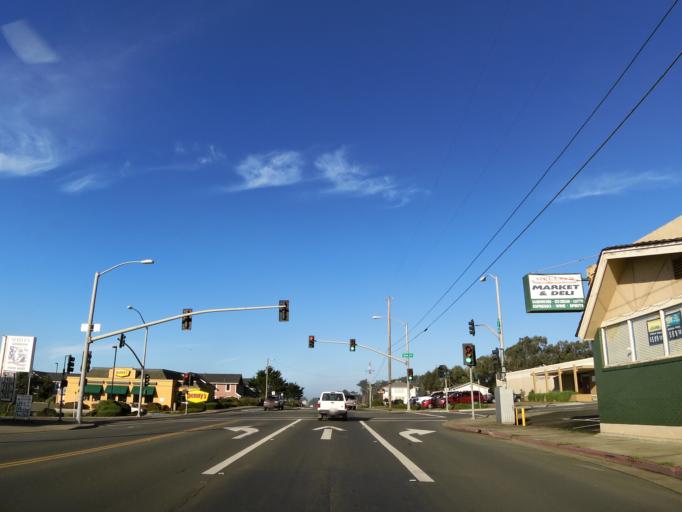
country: US
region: California
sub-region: Mendocino County
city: Fort Bragg
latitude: 39.4515
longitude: -123.8059
